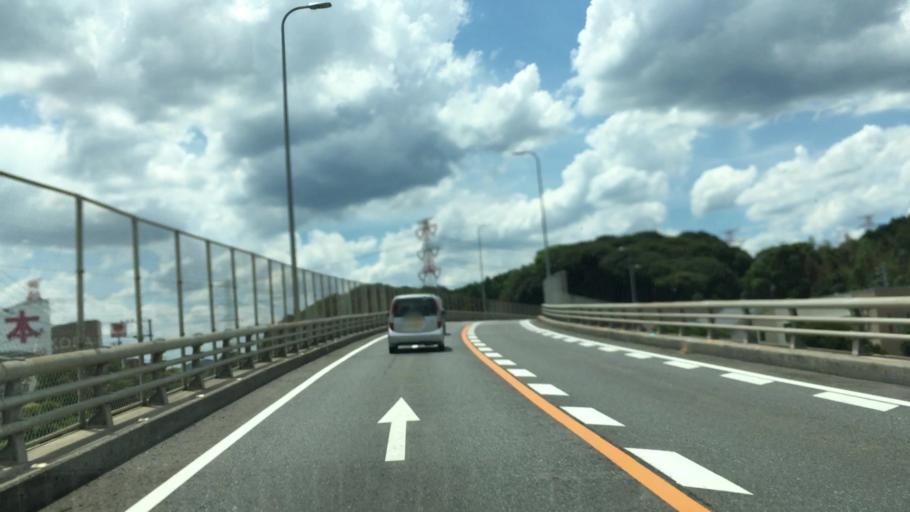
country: JP
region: Fukuoka
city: Chikushino-shi
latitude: 33.4452
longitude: 130.5379
